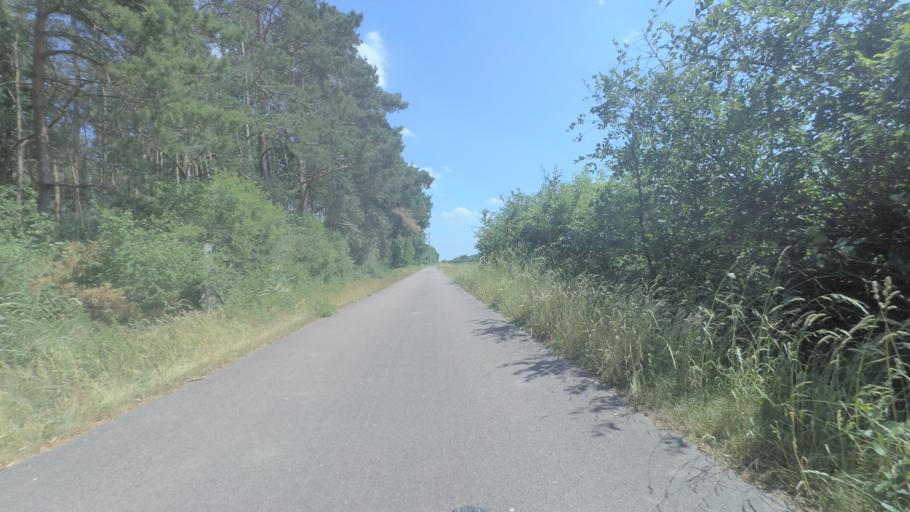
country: DE
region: Saxony-Anhalt
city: Bergwitz
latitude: 51.8224
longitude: 12.5997
